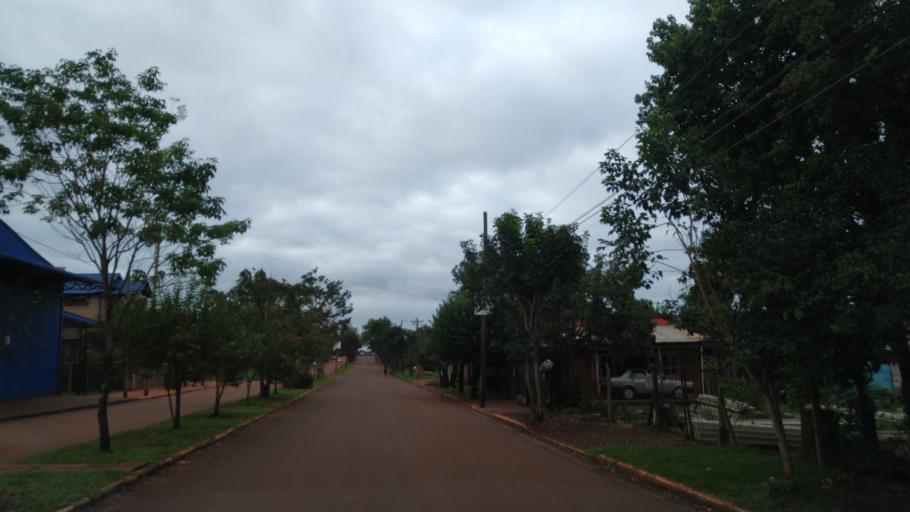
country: AR
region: Misiones
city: Jardin America
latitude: -27.0355
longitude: -55.2349
